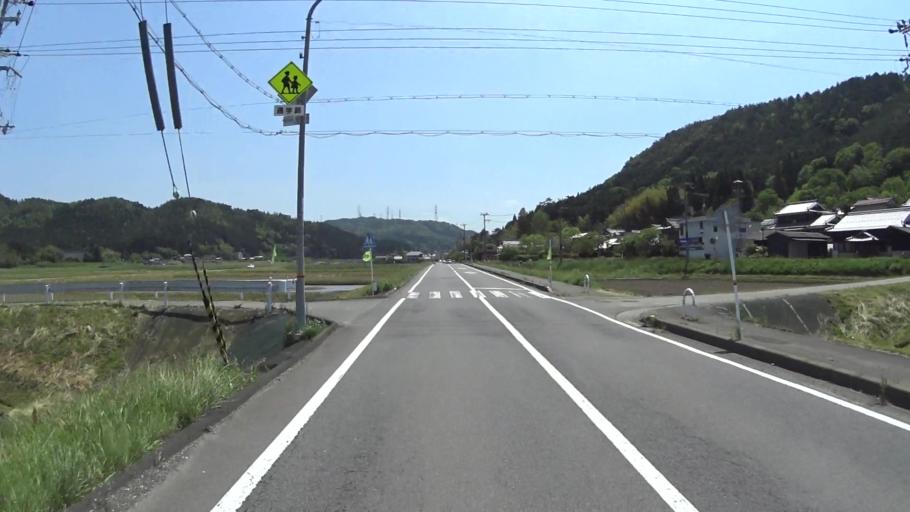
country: JP
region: Kyoto
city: Kameoka
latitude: 35.0209
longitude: 135.4876
